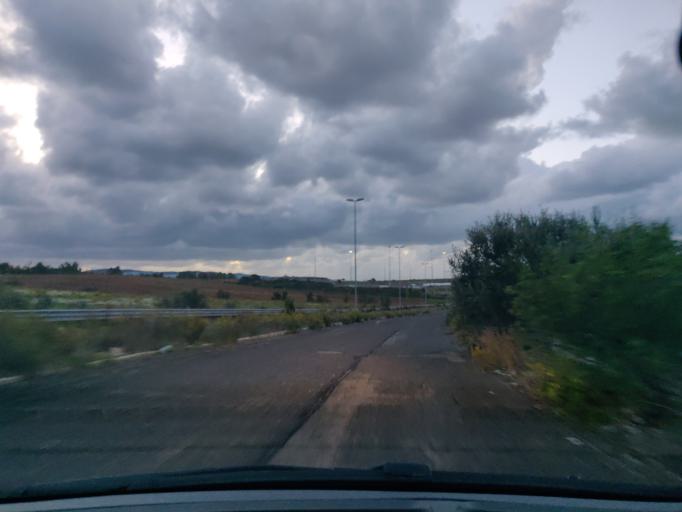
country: IT
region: Latium
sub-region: Citta metropolitana di Roma Capitale
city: Aurelia
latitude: 42.1318
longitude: 11.7765
